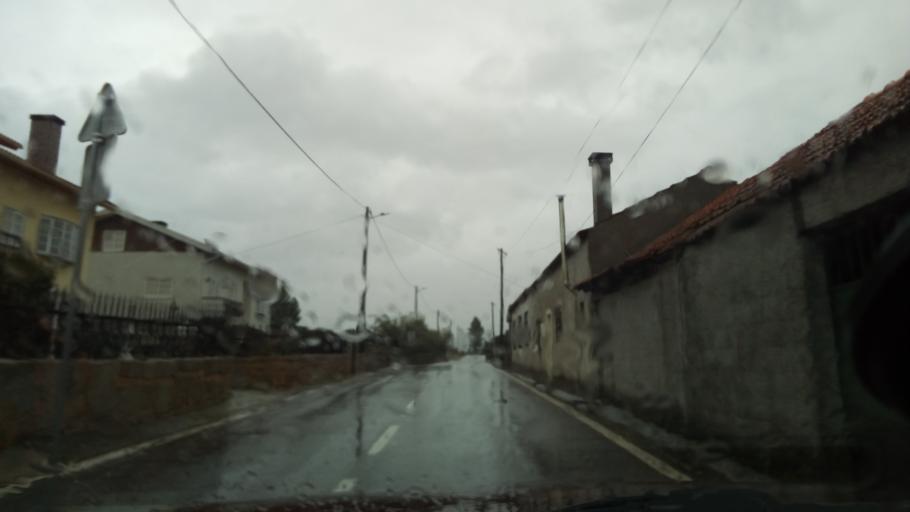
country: PT
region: Guarda
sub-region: Fornos de Algodres
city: Fornos de Algodres
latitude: 40.5531
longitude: -7.5252
